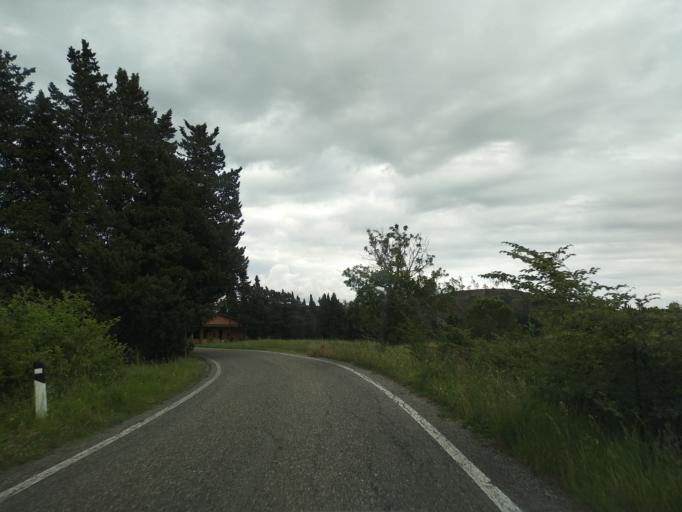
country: IT
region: Tuscany
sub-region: Provincia di Livorno
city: Collesalvetti
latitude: 43.5404
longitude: 10.4534
